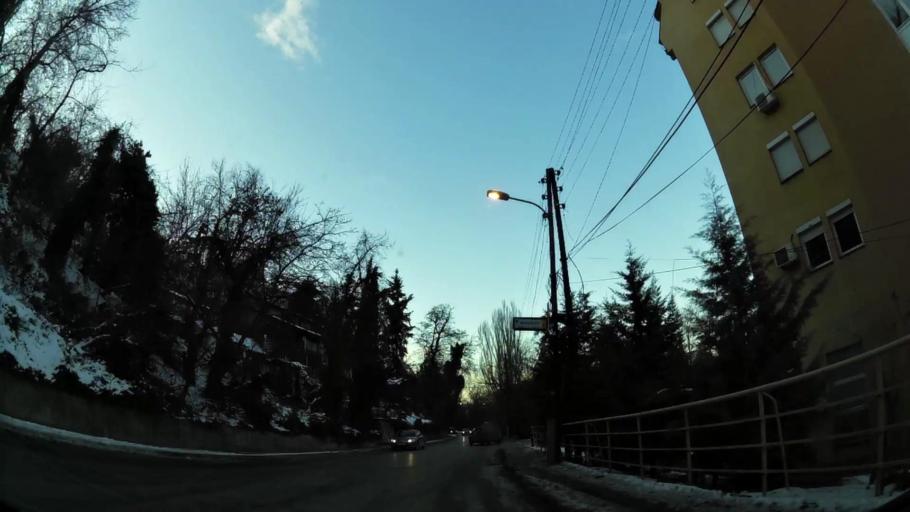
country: MK
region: Karpos
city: Skopje
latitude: 41.9921
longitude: 21.4116
